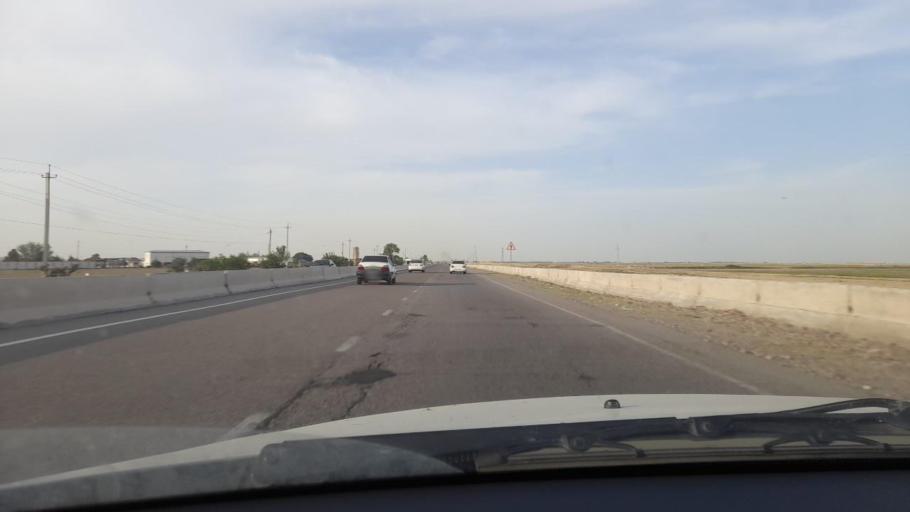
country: UZ
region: Jizzax
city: Gagarin
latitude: 40.4541
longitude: 68.2534
